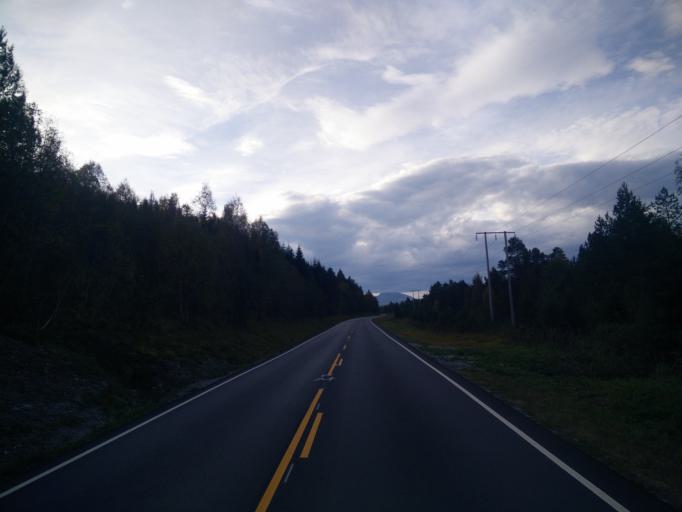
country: NO
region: More og Romsdal
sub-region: Gjemnes
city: Batnfjordsora
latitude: 62.8475
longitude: 7.5975
